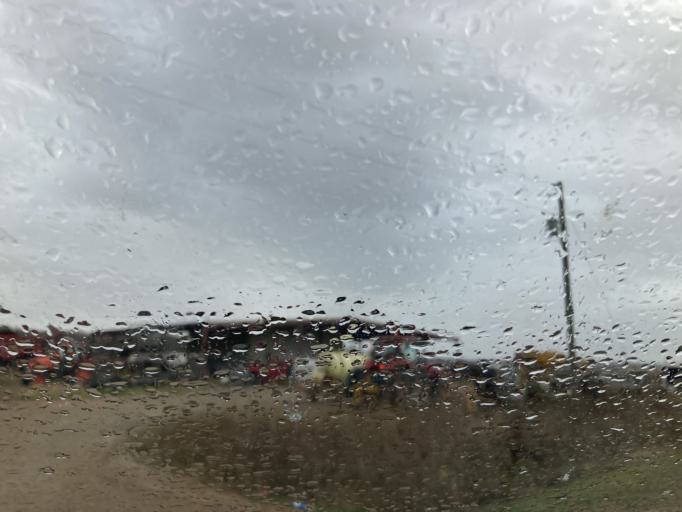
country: US
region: Mississippi
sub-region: Yazoo County
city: Yazoo City
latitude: 32.9868
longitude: -90.4484
